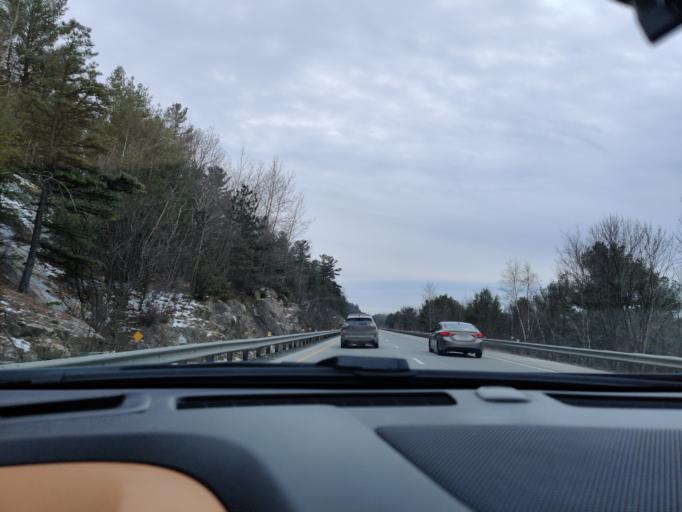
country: US
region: New York
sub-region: Jefferson County
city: Alexandria Bay
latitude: 44.4146
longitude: -75.9218
